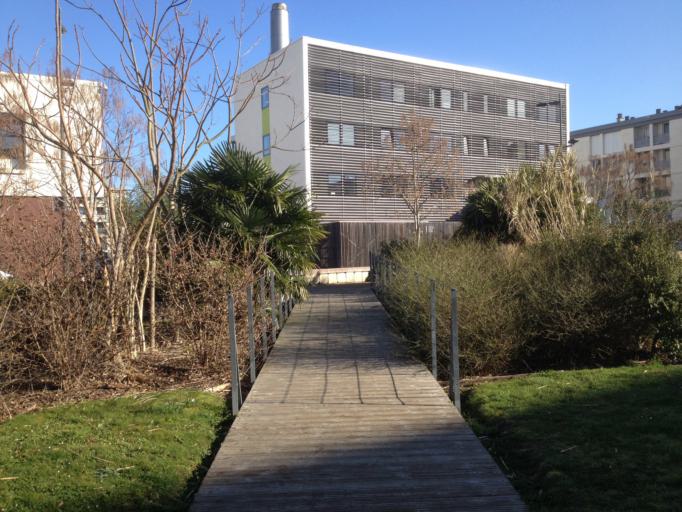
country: FR
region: Centre
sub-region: Departement d'Indre-et-Loire
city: Tours
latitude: 47.3831
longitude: 0.6983
